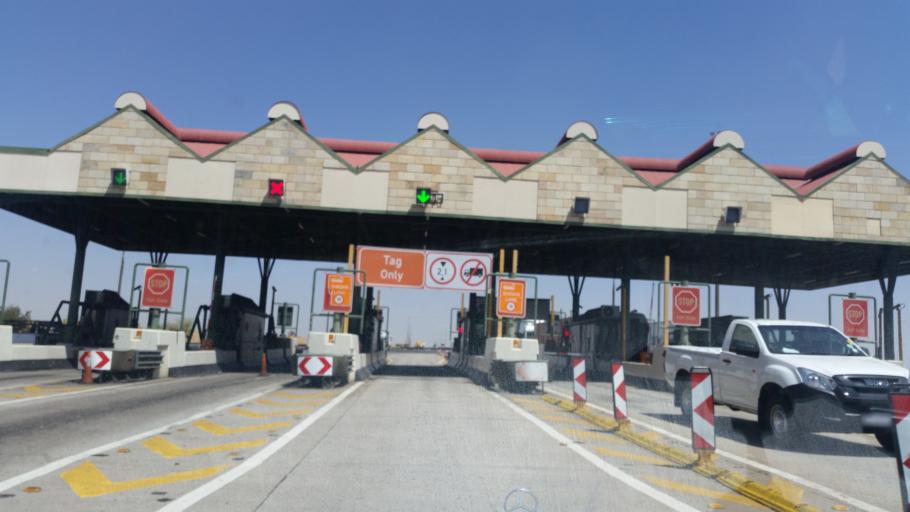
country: ZA
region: Orange Free State
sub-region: Lejweleputswa District Municipality
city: Brandfort
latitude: -28.7986
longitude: 26.6908
